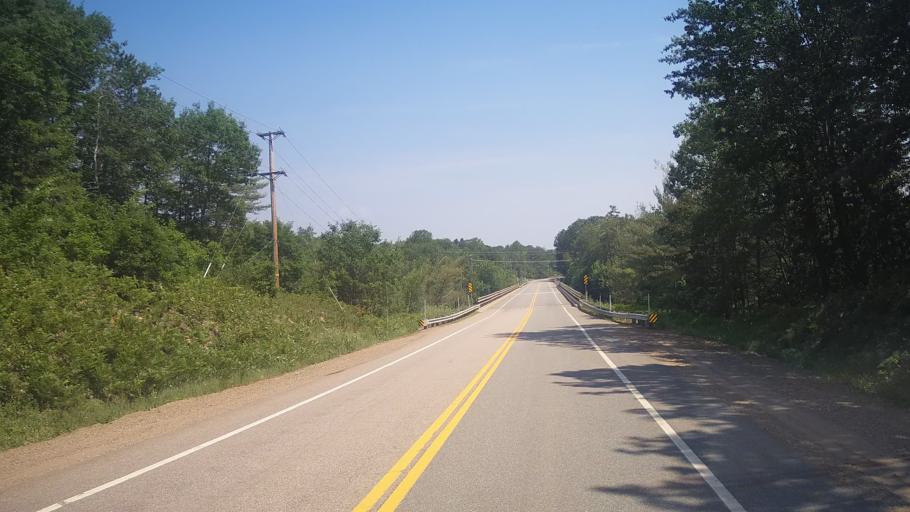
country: CA
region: Quebec
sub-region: Outaouais
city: Fort-Coulonge
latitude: 45.9158
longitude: -76.9260
